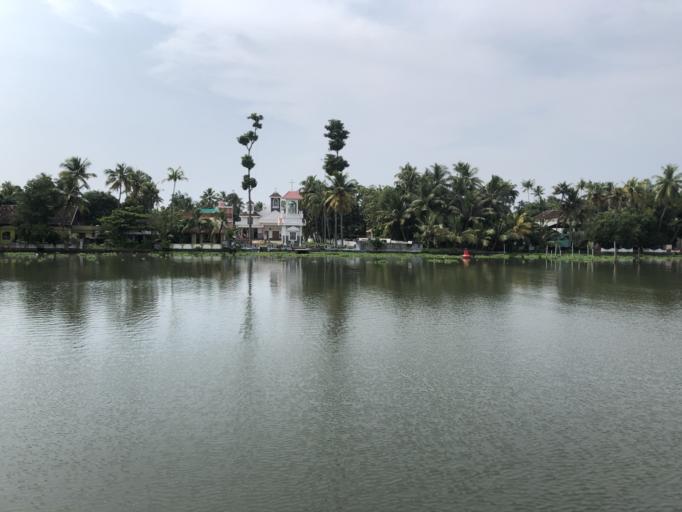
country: IN
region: Kerala
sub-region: Ernakulam
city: Cochin
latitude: 9.9956
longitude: 76.2662
